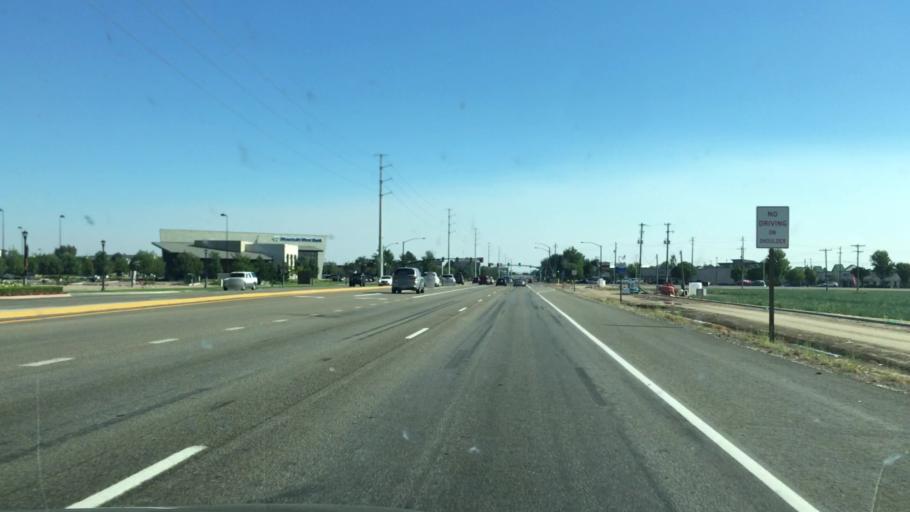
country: US
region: Idaho
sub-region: Ada County
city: Meridian
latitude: 43.6218
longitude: -116.3547
